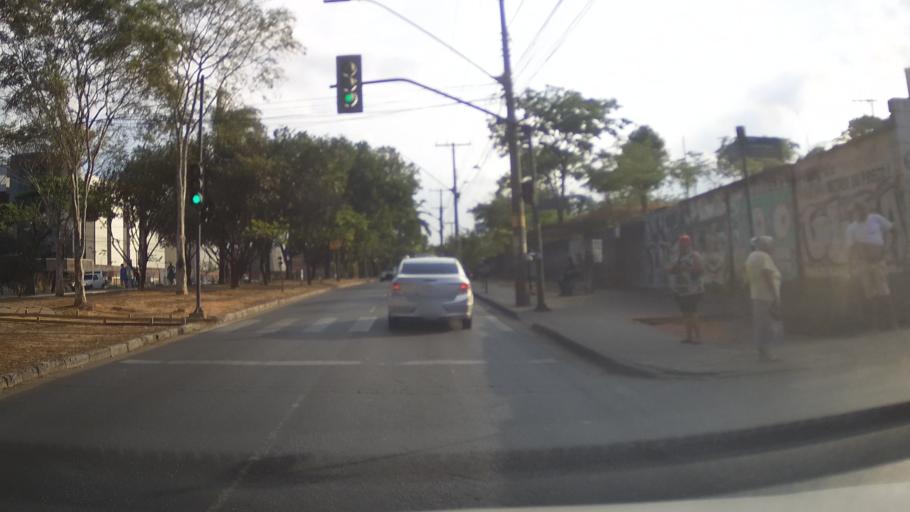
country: BR
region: Minas Gerais
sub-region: Belo Horizonte
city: Belo Horizonte
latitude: -19.8828
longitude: -43.9152
